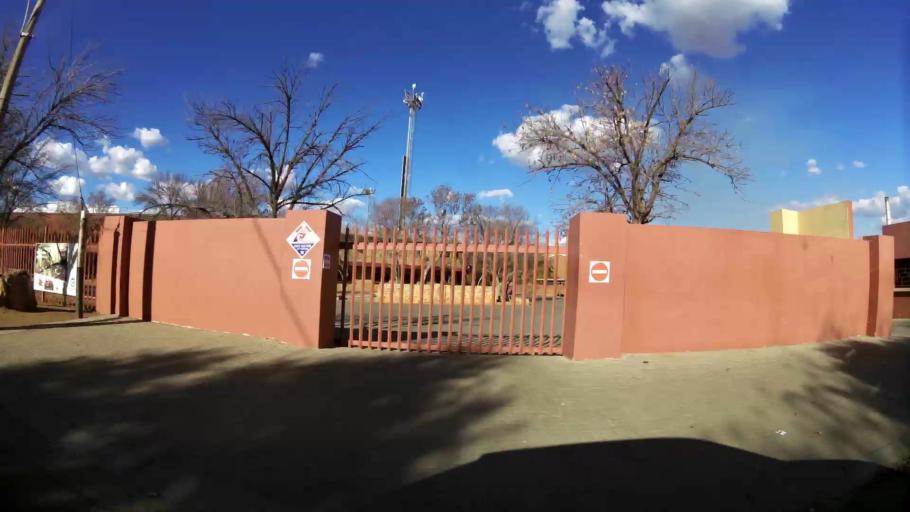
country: ZA
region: North-West
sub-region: Dr Kenneth Kaunda District Municipality
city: Klerksdorp
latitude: -26.8424
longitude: 26.6620
